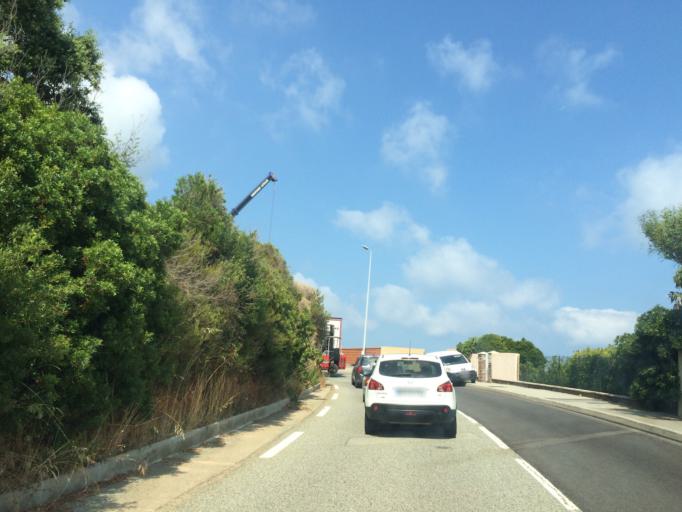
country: FR
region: Provence-Alpes-Cote d'Azur
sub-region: Departement des Alpes-Maritimes
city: Theoule-sur-Mer
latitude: 43.4382
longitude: 6.8954
